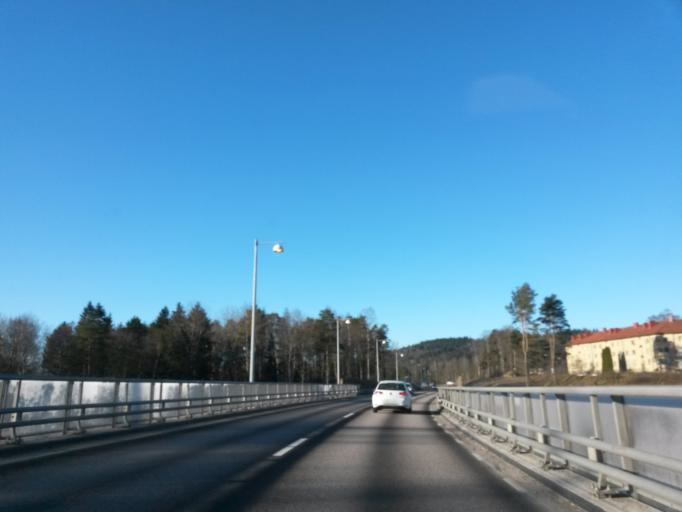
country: SE
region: Vaestra Goetaland
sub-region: Boras Kommun
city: Boras
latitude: 57.7436
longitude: 12.9448
